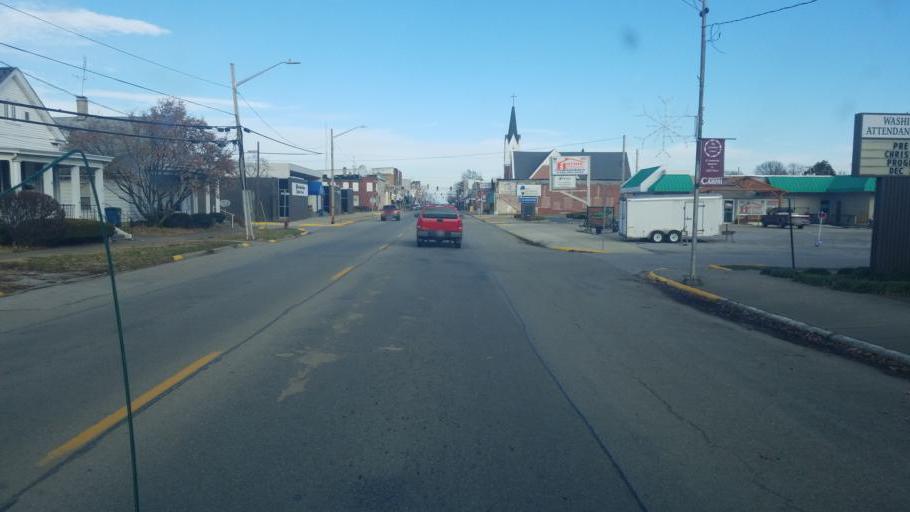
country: US
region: Illinois
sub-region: White County
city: Carmi
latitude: 38.0883
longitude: -88.1628
